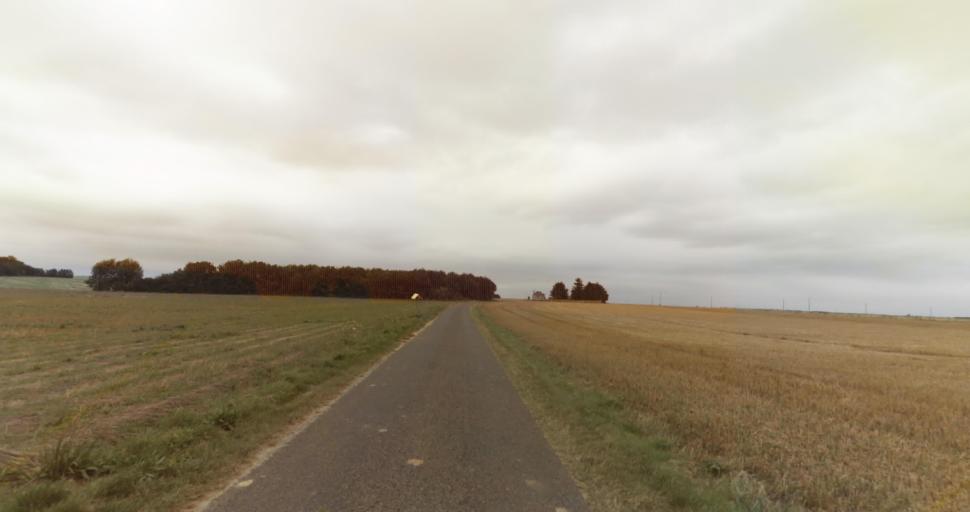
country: FR
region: Haute-Normandie
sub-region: Departement de l'Eure
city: La Couture-Boussey
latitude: 48.9172
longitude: 1.3547
